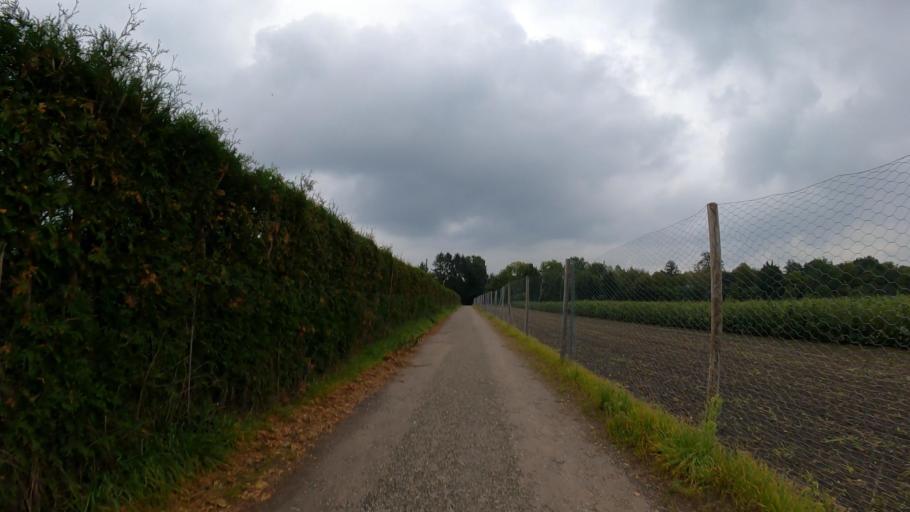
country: DE
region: Schleswig-Holstein
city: Halstenbek
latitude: 53.6326
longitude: 9.8309
